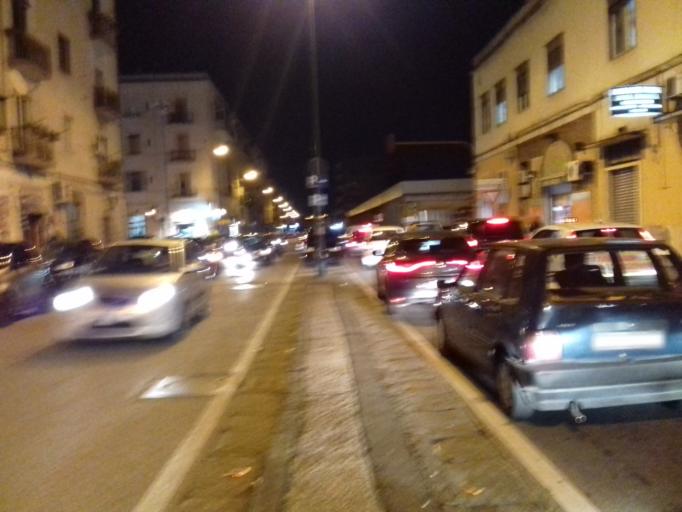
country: IT
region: Campania
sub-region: Provincia di Napoli
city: Napoli
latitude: 40.8559
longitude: 14.2877
